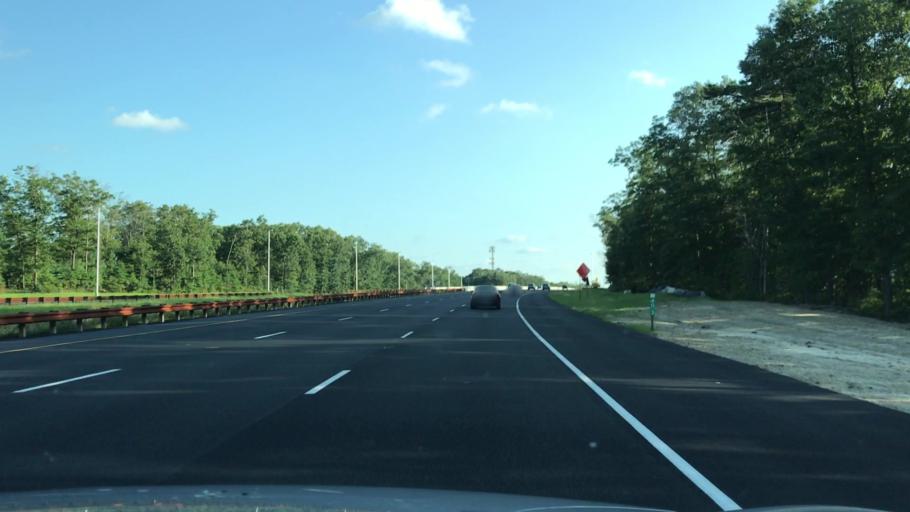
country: US
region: New Jersey
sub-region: Atlantic County
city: Pomona
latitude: 39.4554
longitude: -74.5352
